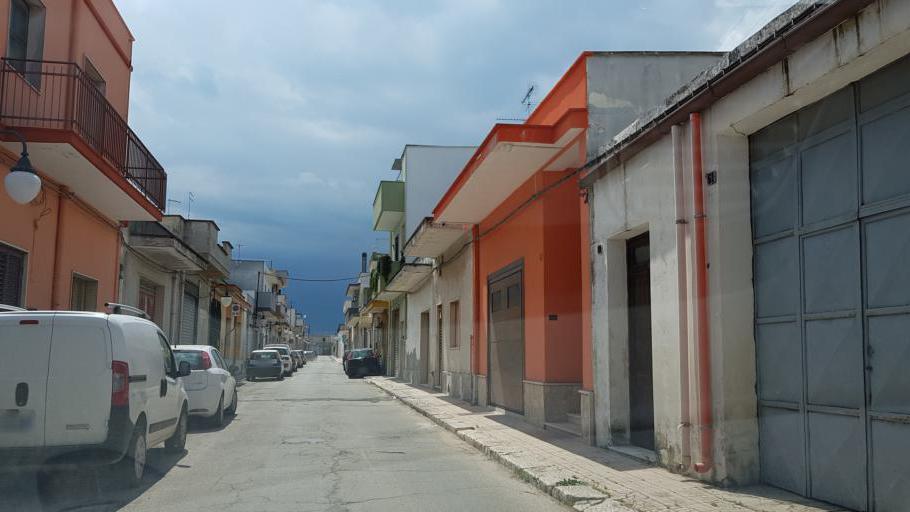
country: IT
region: Apulia
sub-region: Provincia di Brindisi
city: Tuturano
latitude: 40.5449
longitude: 17.9509
